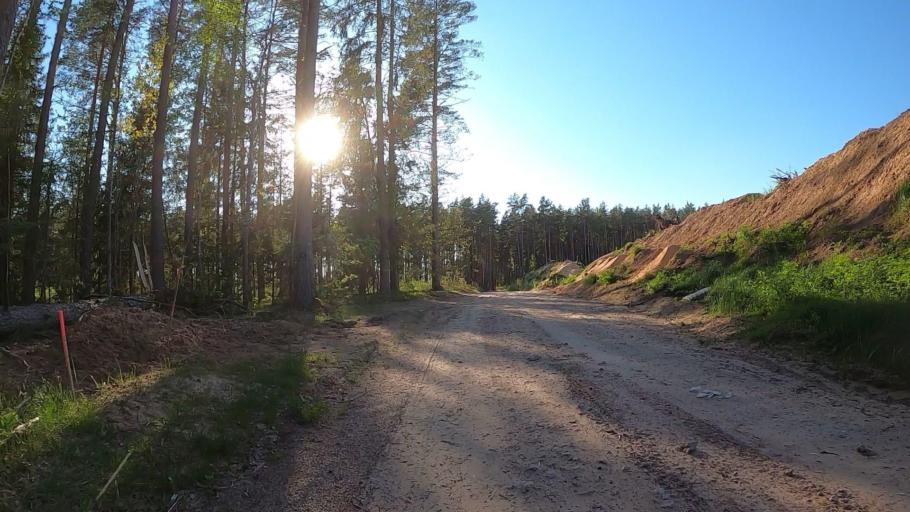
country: LV
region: Kekava
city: Kekava
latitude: 56.7811
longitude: 24.3087
